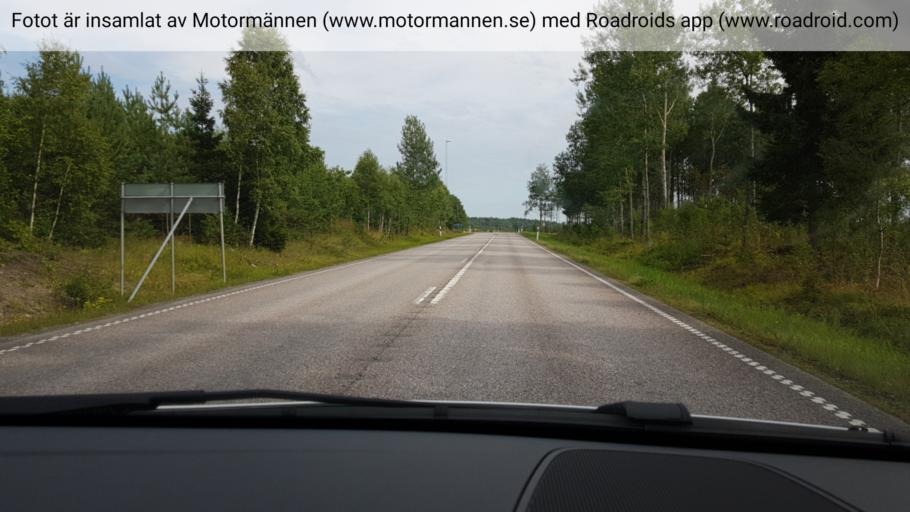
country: SE
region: Stockholm
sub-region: Norrtalje Kommun
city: Hallstavik
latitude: 60.0428
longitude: 18.5410
